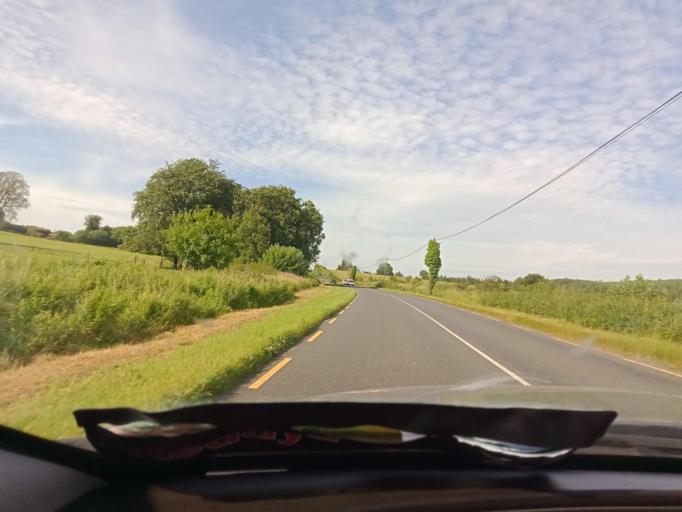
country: IE
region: Leinster
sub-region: An Iarmhi
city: An Muileann gCearr
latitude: 53.5603
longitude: -7.3249
